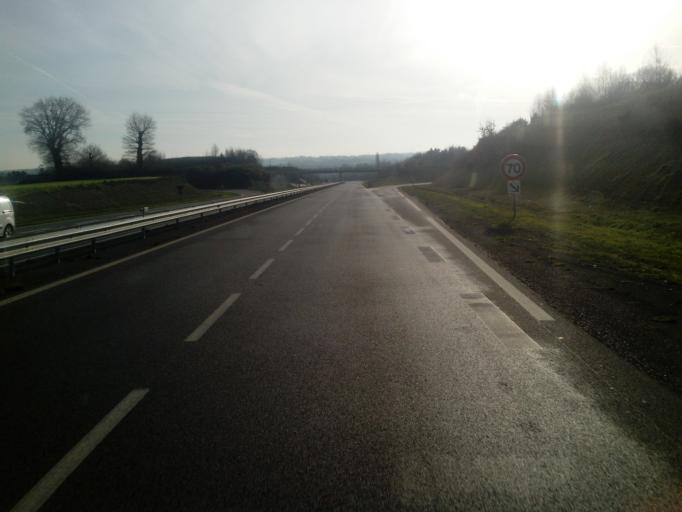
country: FR
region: Brittany
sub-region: Departement d'Ille-et-Vilaine
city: Chevaigne
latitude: 48.2122
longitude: -1.6238
